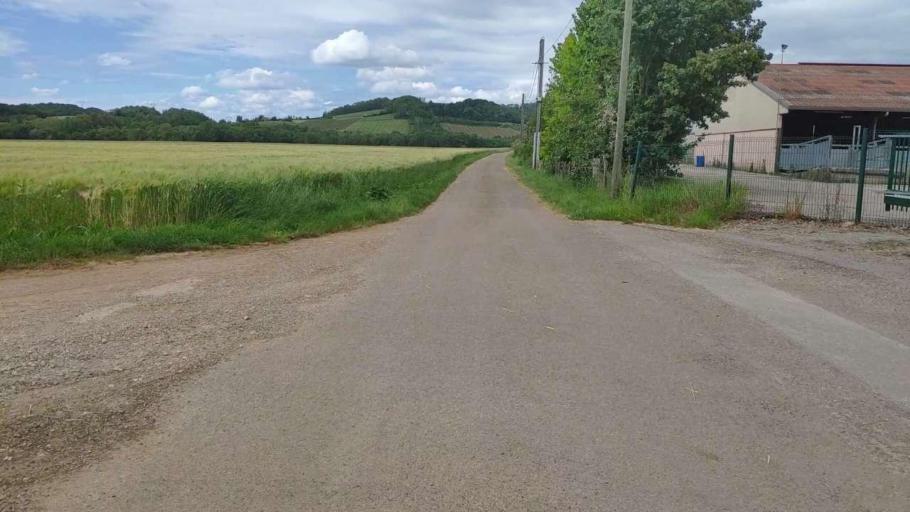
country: FR
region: Franche-Comte
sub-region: Departement du Jura
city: Montmorot
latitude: 46.7641
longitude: 5.5637
